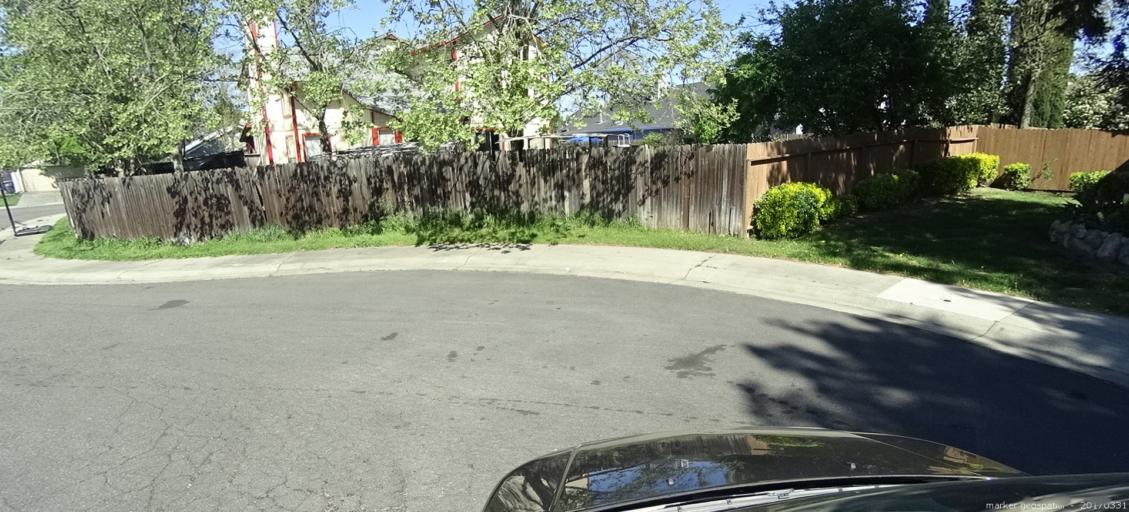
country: US
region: California
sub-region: Sacramento County
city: Laguna
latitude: 38.4585
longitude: -121.4333
